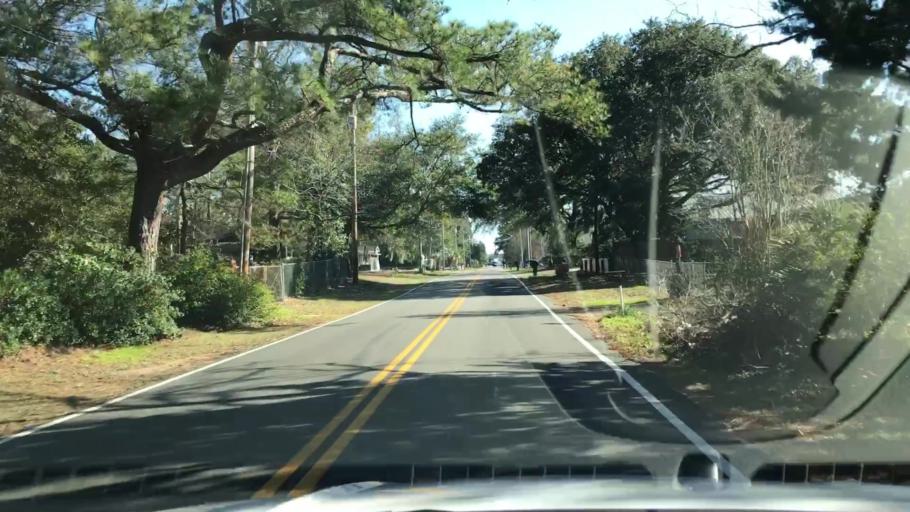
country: US
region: South Carolina
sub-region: Horry County
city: Garden City
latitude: 33.5910
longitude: -78.9976
